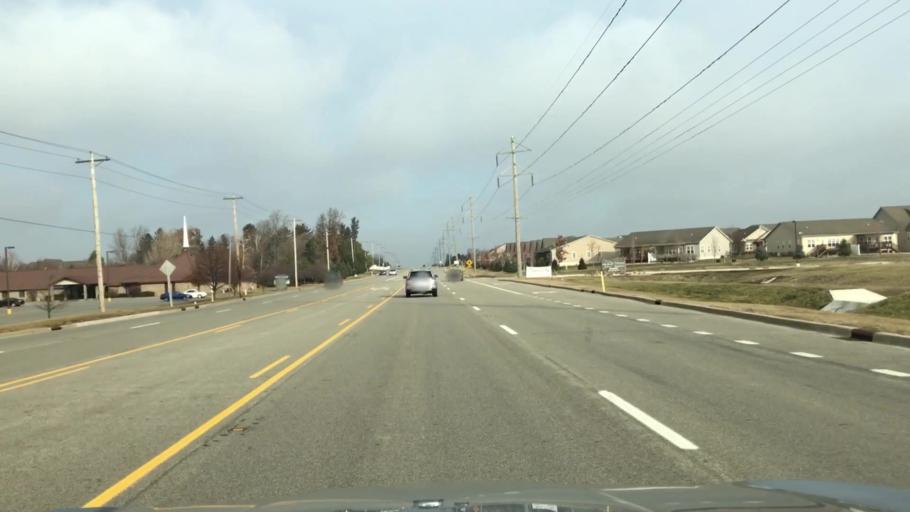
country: US
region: Illinois
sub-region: McLean County
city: Normal
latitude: 40.5045
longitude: -88.9027
